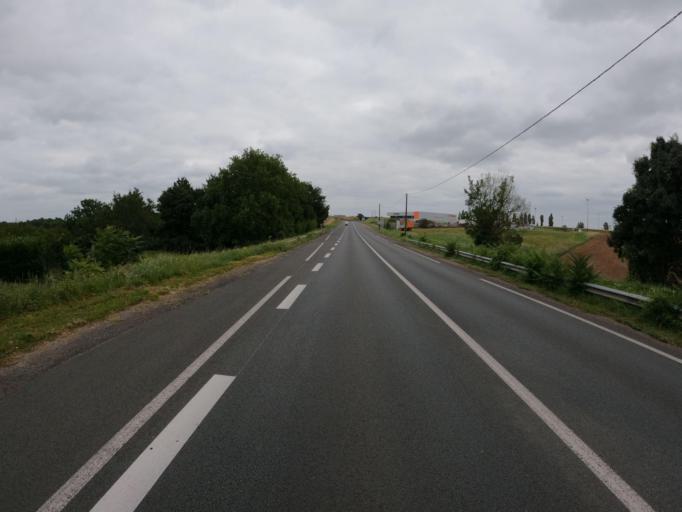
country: FR
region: Pays de la Loire
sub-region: Departement de la Vendee
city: Serigne
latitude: 46.4696
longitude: -0.8524
